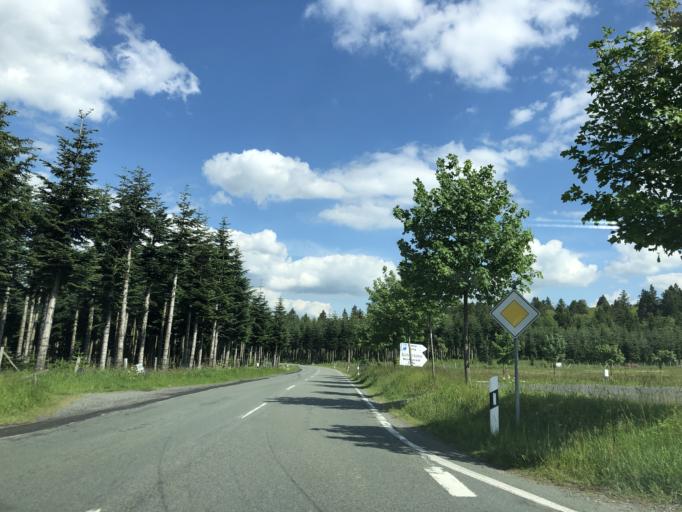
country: DE
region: North Rhine-Westphalia
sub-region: Regierungsbezirk Arnsberg
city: Winterberg
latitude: 51.1859
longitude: 8.4788
